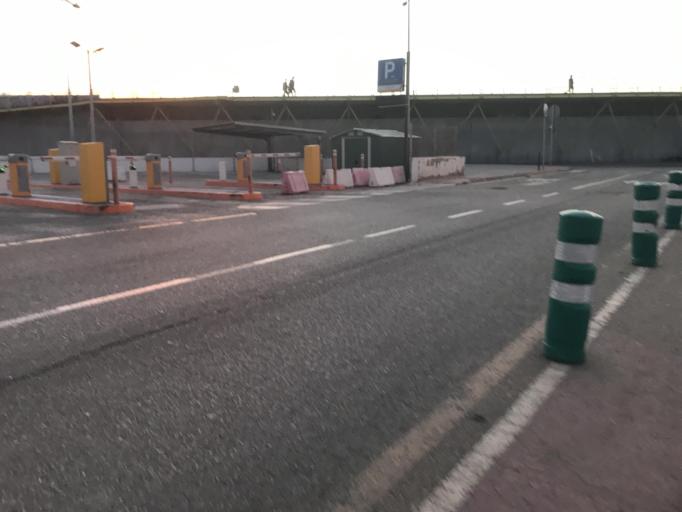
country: ES
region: Valencia
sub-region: Provincia de Alicante
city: Torrevieja
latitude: 37.9732
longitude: -0.6791
